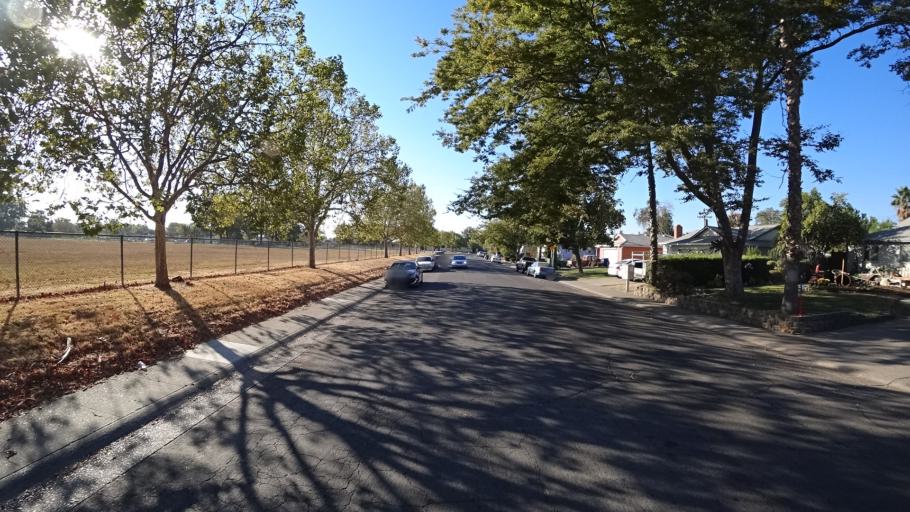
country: US
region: California
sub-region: Sacramento County
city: Parkway
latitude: 38.4804
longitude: -121.4946
